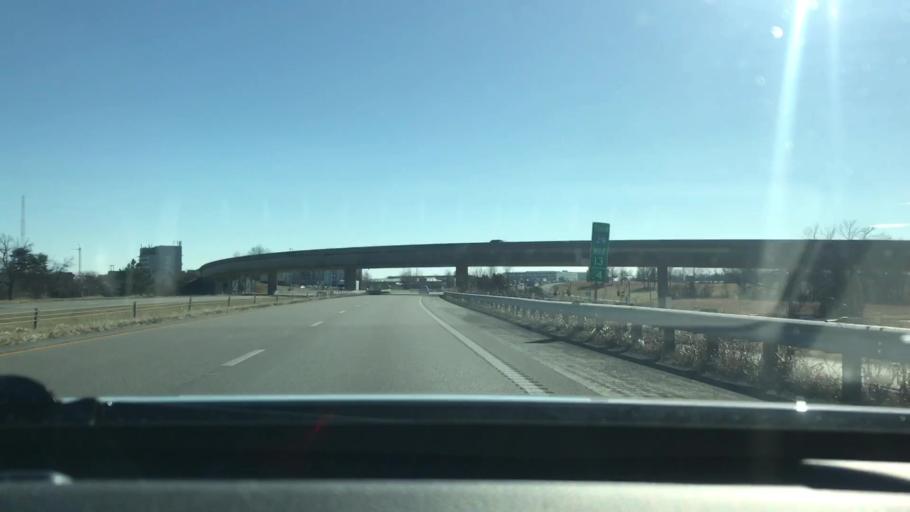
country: US
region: Missouri
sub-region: Platte County
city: Weatherby Lake
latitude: 39.3127
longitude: -94.6891
